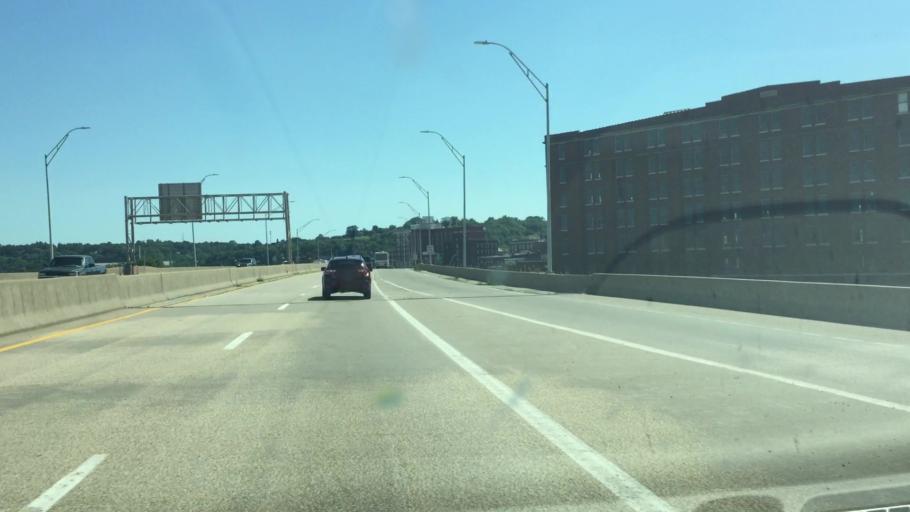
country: US
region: Iowa
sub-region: Dubuque County
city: Dubuque
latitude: 42.5016
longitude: -90.6616
